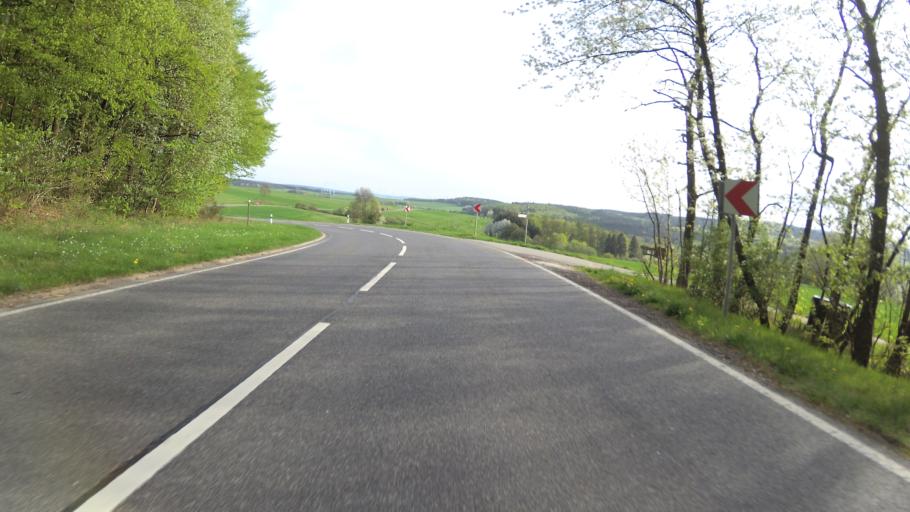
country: DE
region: Rheinland-Pfalz
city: Longkamp
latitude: 49.8705
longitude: 7.1135
